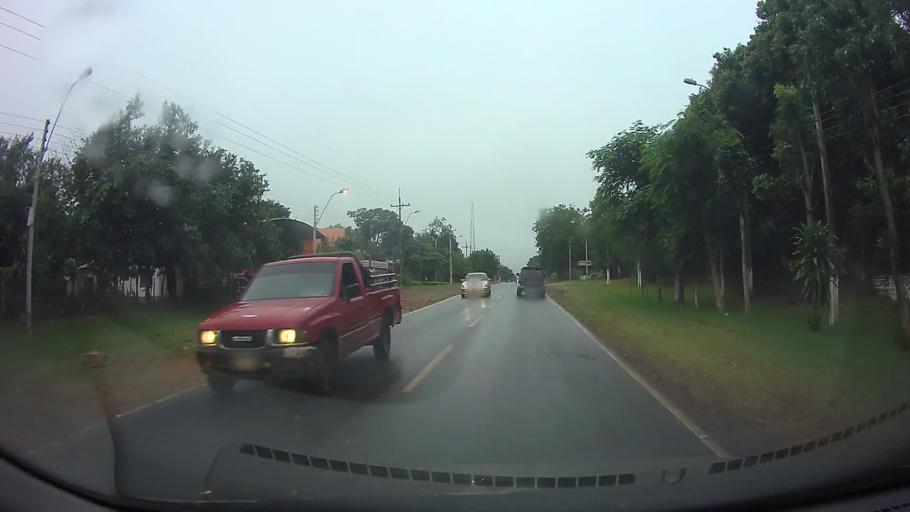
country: PY
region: Central
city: Ita
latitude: -25.4544
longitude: -57.3679
